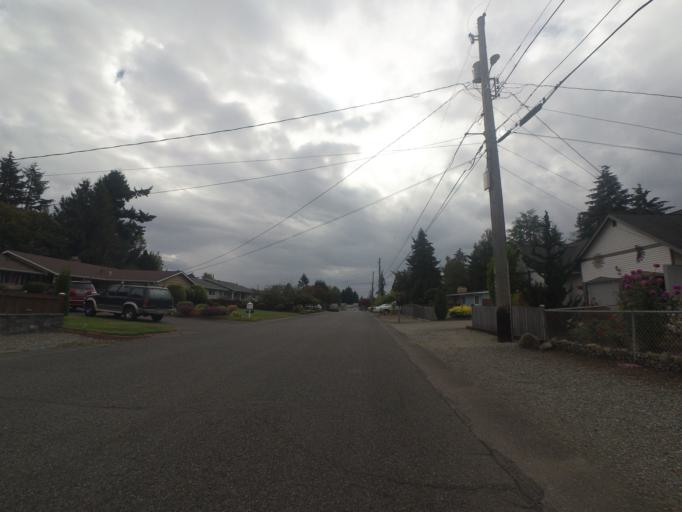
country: US
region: Washington
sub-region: Pierce County
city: University Place
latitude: 47.2159
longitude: -122.5420
